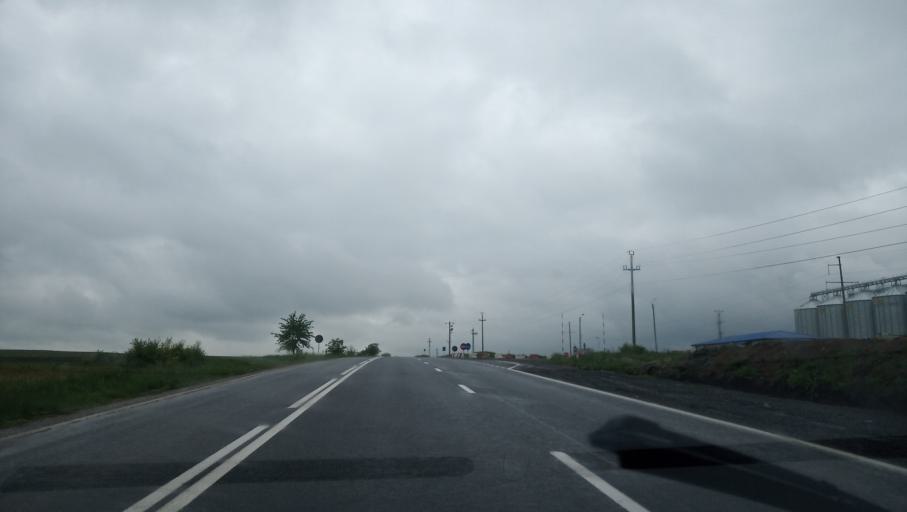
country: RO
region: Alba
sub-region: Comuna Cut
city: Cut
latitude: 45.9179
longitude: 23.7076
